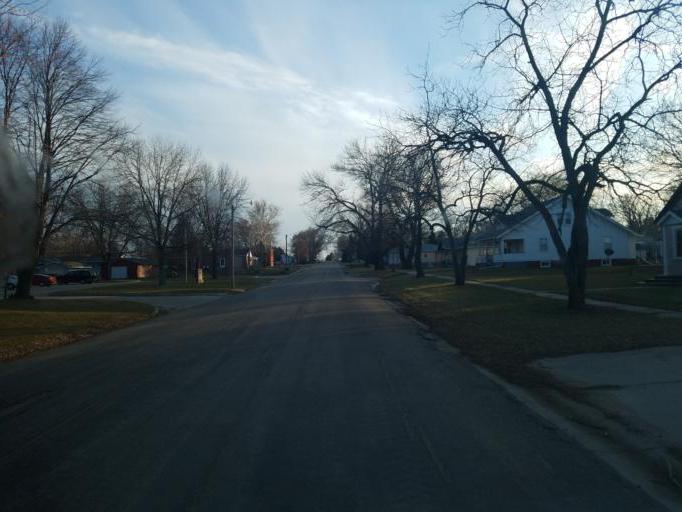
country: US
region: South Dakota
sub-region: Yankton County
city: Yankton
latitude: 42.7301
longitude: -97.4946
